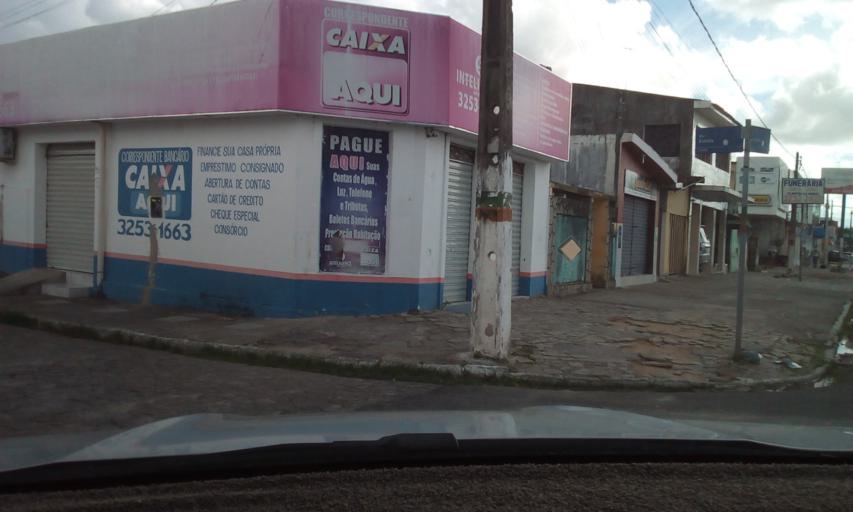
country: BR
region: Paraiba
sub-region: Bayeux
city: Bayeux
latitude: -7.1244
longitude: -34.9223
